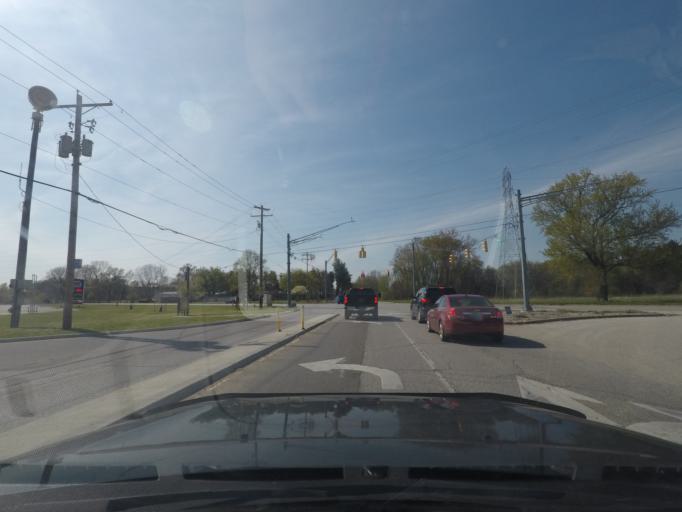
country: US
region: Indiana
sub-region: Saint Joseph County
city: Osceola
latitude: 41.7241
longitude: -86.0398
